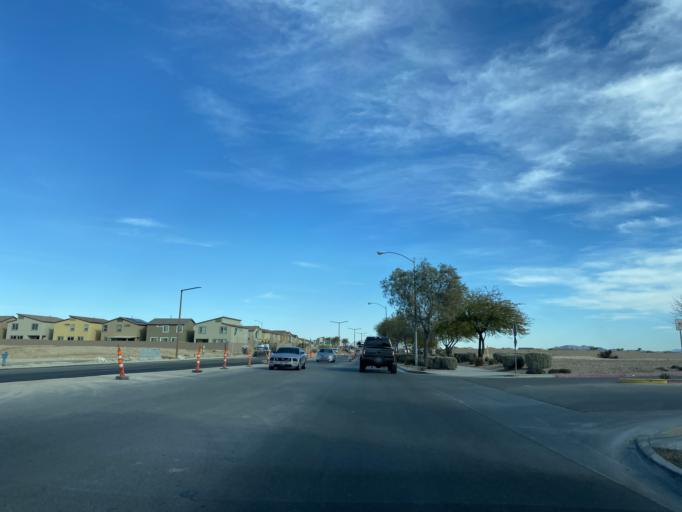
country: US
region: Nevada
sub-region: Clark County
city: North Las Vegas
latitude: 36.2912
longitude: -115.2041
